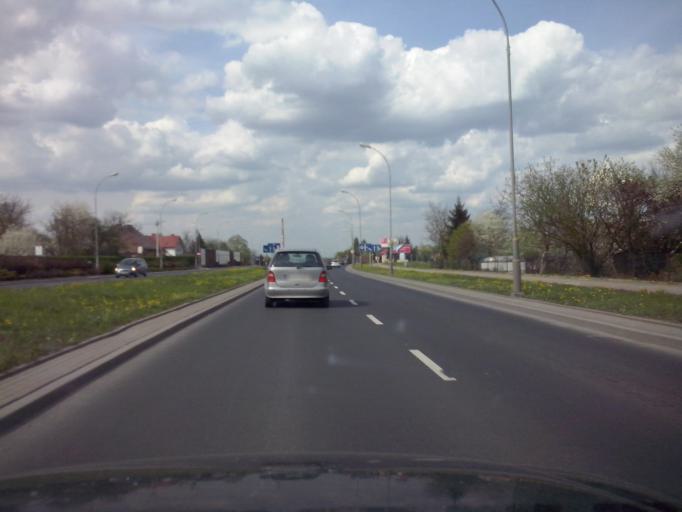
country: PL
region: Subcarpathian Voivodeship
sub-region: Rzeszow
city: Rzeszow
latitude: 50.0403
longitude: 22.0325
